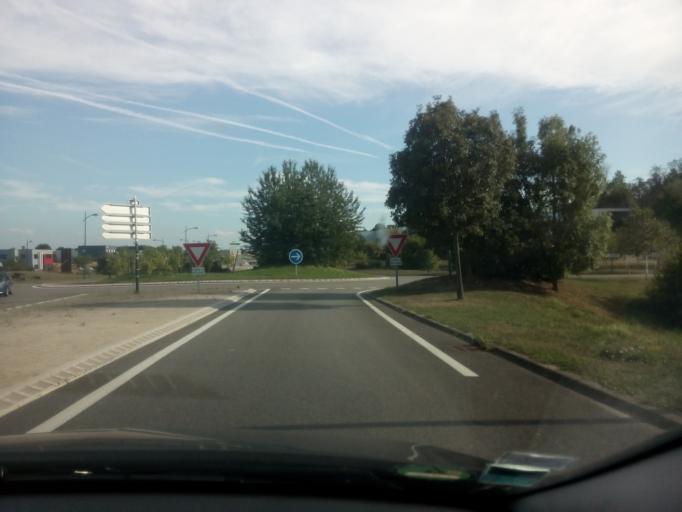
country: FR
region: Alsace
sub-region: Departement du Bas-Rhin
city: Wissembourg
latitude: 49.0222
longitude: 7.9650
